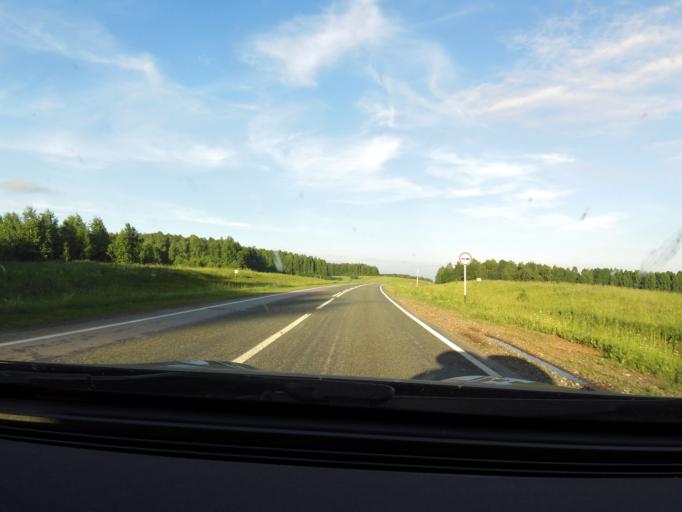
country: RU
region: Perm
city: Siva
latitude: 58.6416
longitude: 53.8347
